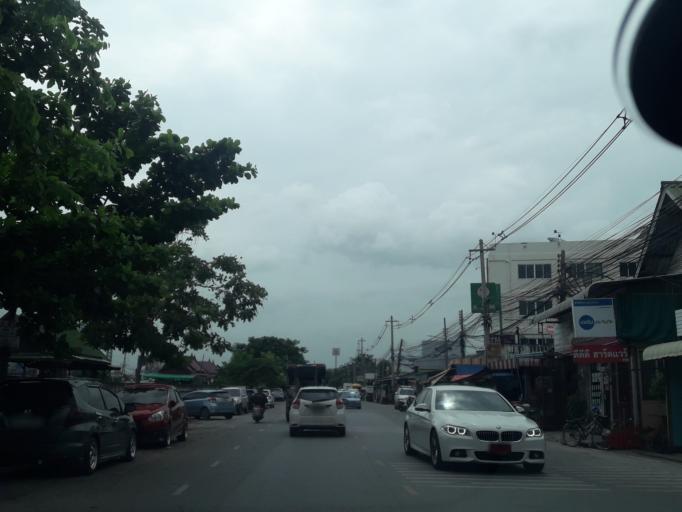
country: TH
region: Bangkok
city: Sai Mai
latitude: 13.9885
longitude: 100.6382
